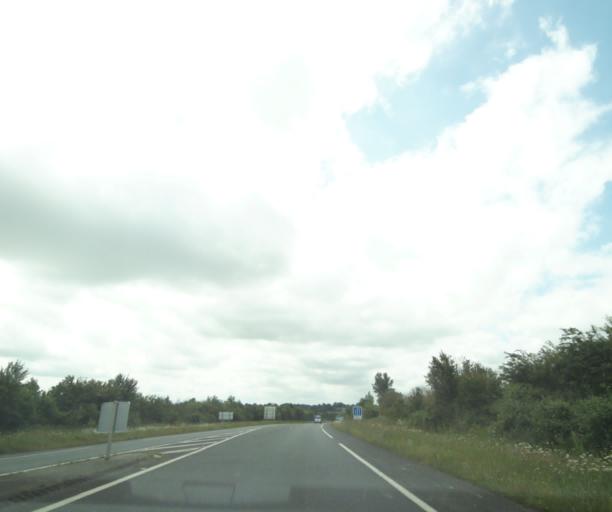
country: FR
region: Poitou-Charentes
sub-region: Departement des Deux-Sevres
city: Viennay
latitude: 46.7731
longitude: -0.2189
